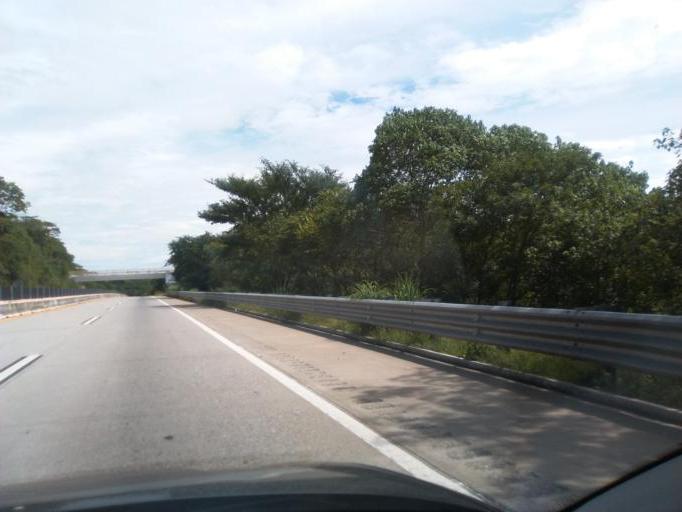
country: MX
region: Guerrero
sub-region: Acapulco de Juarez
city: Pueblo Madero (El Playon)
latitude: 17.0748
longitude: -99.6142
